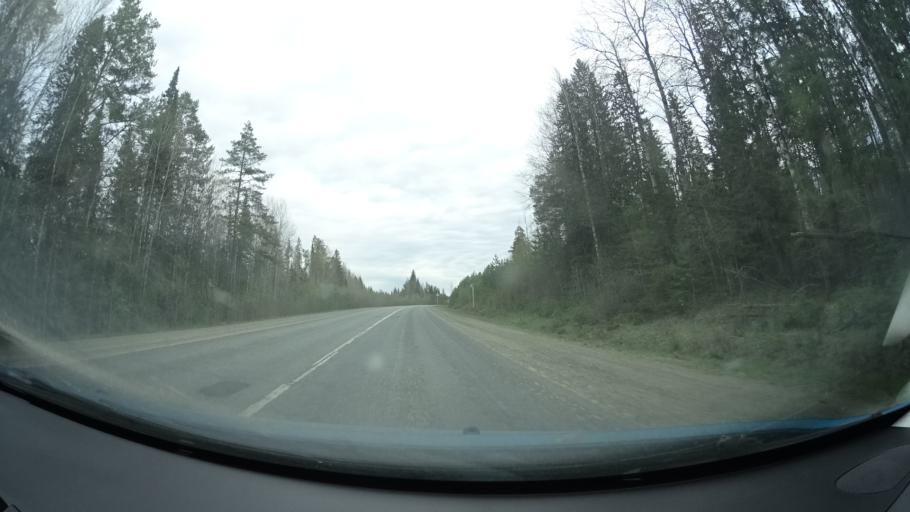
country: RU
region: Perm
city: Yugo-Kamskiy
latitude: 57.6616
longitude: 55.5954
